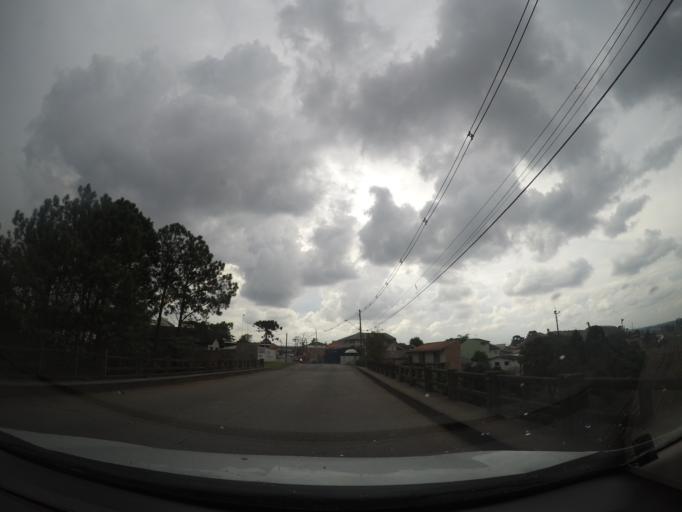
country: BR
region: Parana
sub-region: Sao Jose Dos Pinhais
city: Sao Jose dos Pinhais
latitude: -25.5449
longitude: -49.2413
